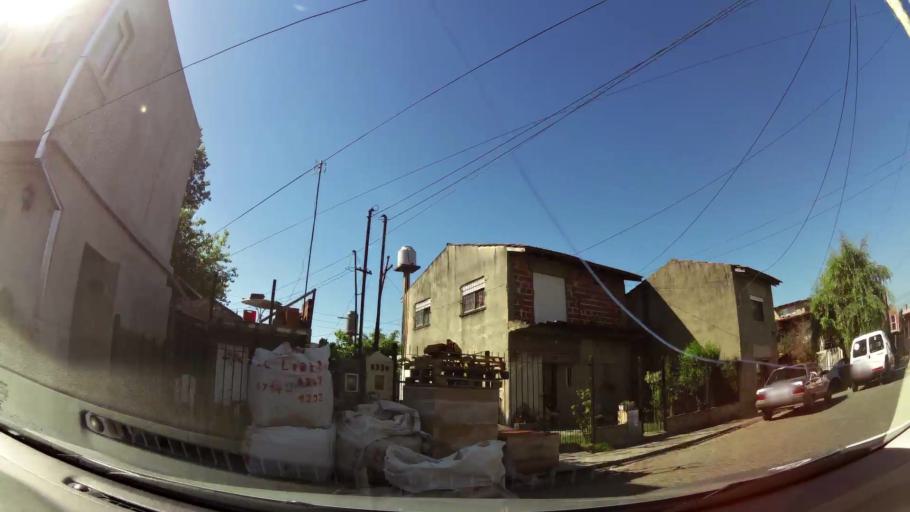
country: AR
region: Buenos Aires
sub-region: Partido de Tigre
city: Tigre
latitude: -34.4757
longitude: -58.5812
